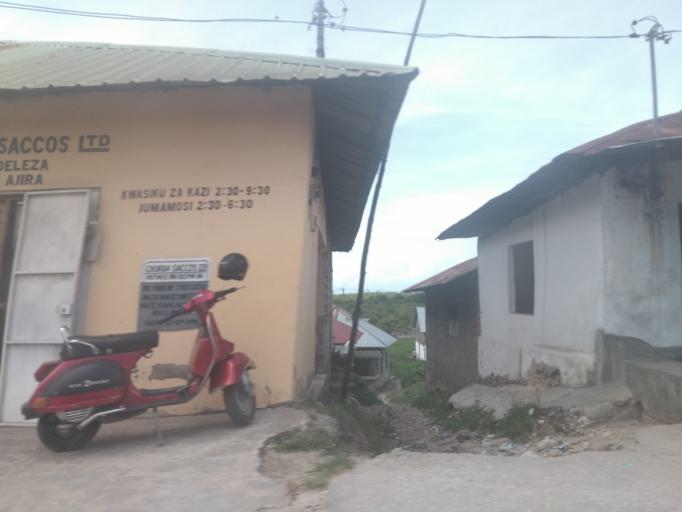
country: TZ
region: Zanzibar Urban/West
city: Zanzibar
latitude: -6.1514
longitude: 39.2096
